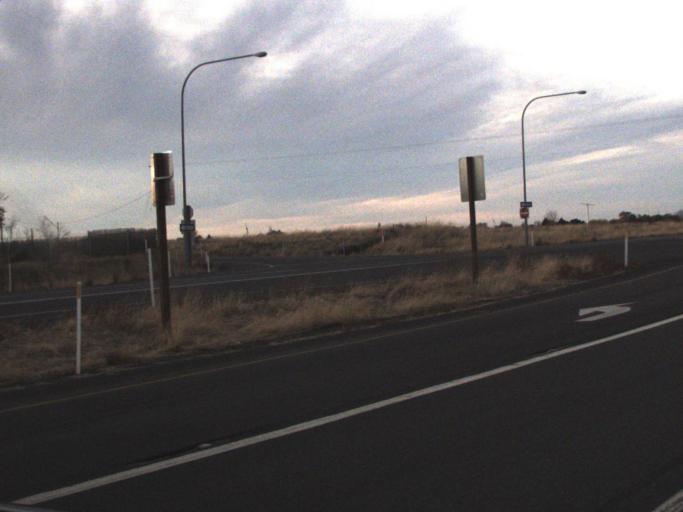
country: US
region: Washington
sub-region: Walla Walla County
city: Burbank
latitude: 46.1752
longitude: -118.9638
